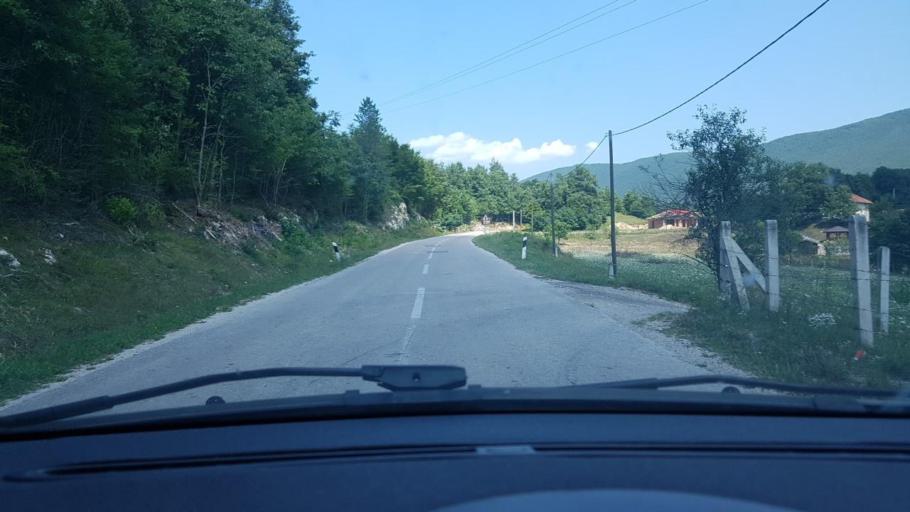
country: BA
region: Federation of Bosnia and Herzegovina
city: Orasac
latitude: 44.6071
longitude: 16.0701
